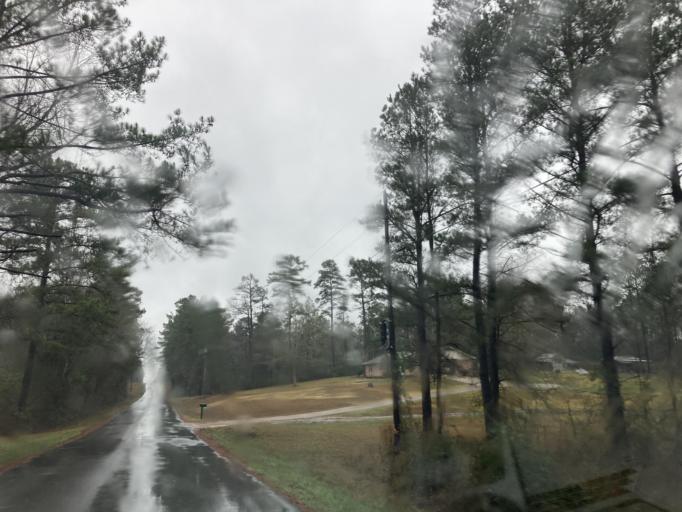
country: US
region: Mississippi
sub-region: Forrest County
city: Rawls Springs
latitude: 31.4693
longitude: -89.3822
